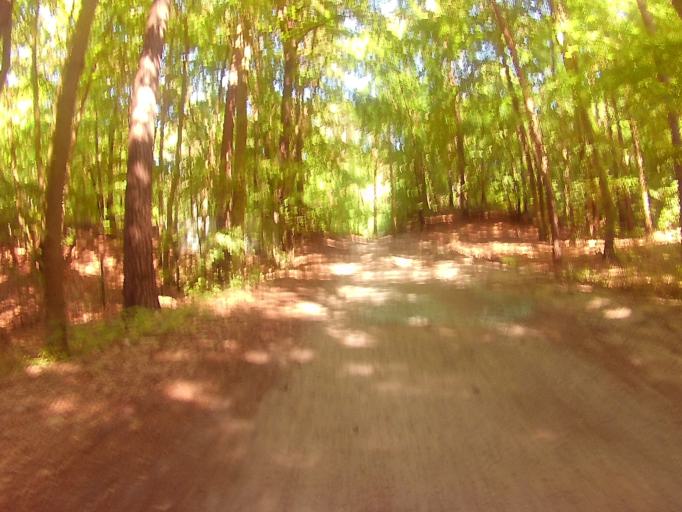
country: DE
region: Mecklenburg-Vorpommern
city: Ostseebad Zinnowitz
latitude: 54.0694
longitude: 13.9553
